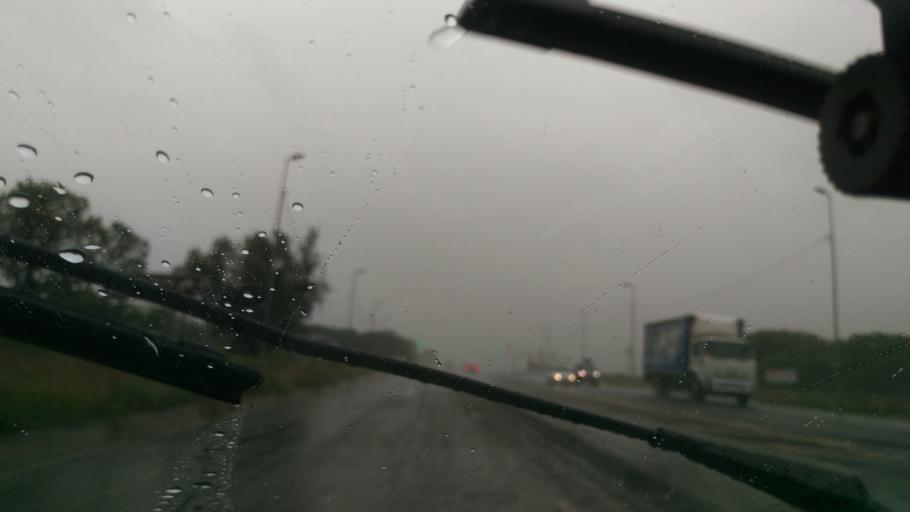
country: ZA
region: Gauteng
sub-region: West Rand District Municipality
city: Muldersdriseloop
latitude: -26.0530
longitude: 27.9484
